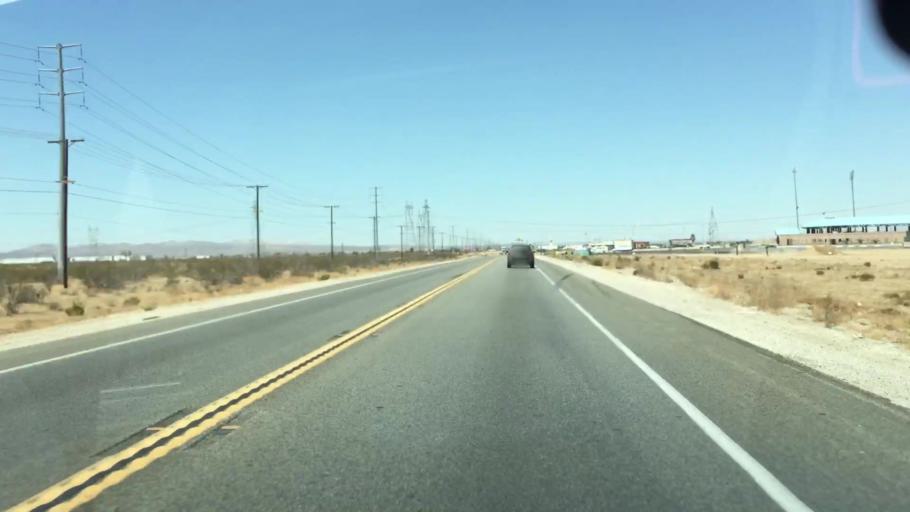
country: US
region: California
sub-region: San Bernardino County
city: Adelanto
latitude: 34.5512
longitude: -117.4025
